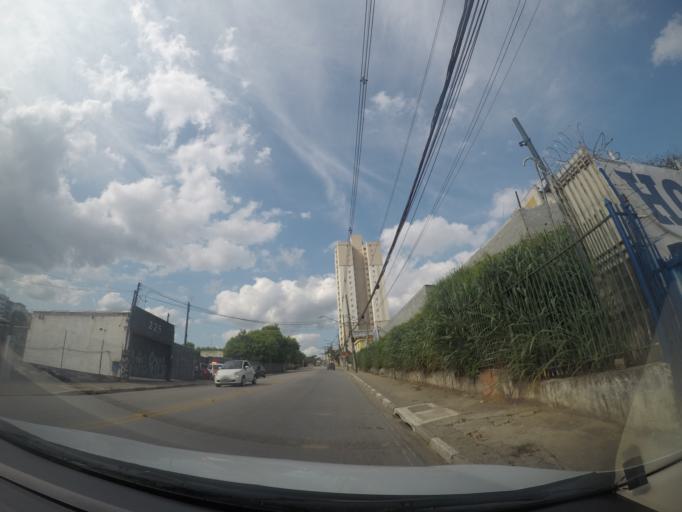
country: BR
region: Sao Paulo
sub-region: Guarulhos
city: Guarulhos
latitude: -23.4631
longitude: -46.5121
